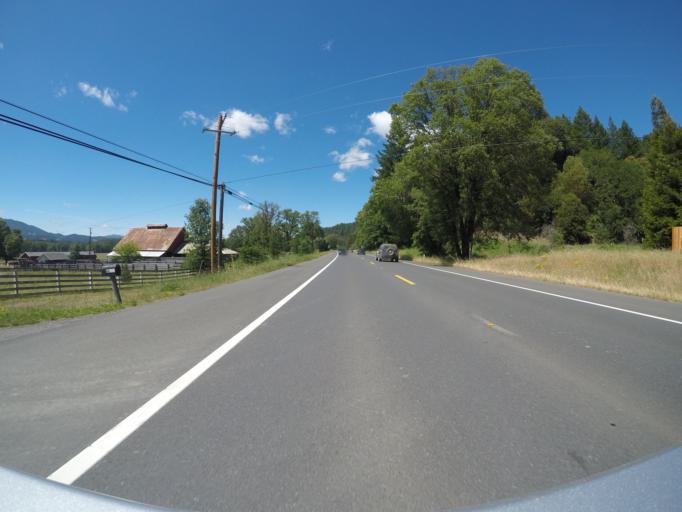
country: US
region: California
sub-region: Mendocino County
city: Laytonville
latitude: 39.6756
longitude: -123.4757
